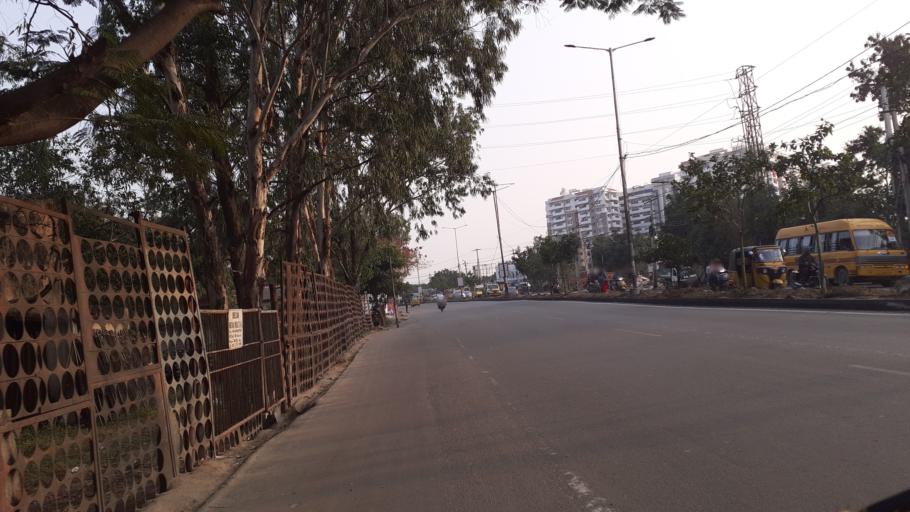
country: IN
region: Telangana
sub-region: Medak
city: Serilingampalle
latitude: 17.4905
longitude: 78.3538
